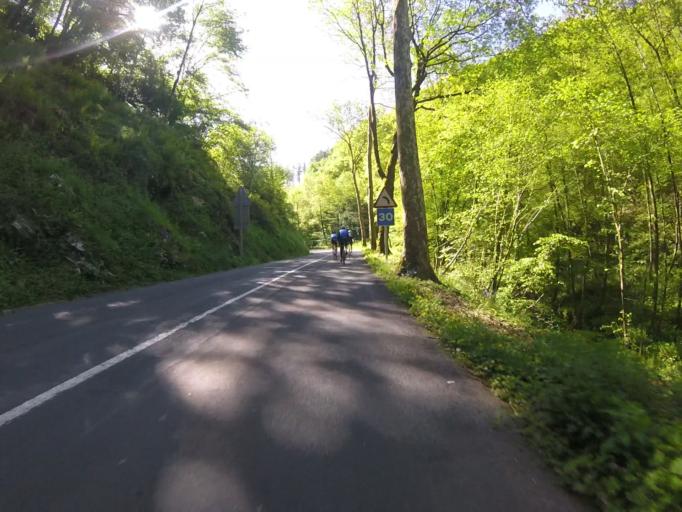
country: ES
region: Basque Country
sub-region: Provincia de Guipuzcoa
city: Errezil
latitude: 43.1742
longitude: -2.2024
